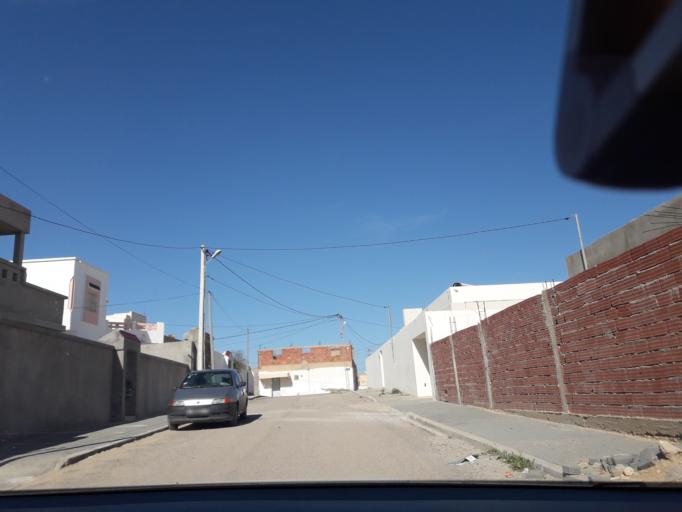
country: TN
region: Safaqis
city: Sfax
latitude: 34.7381
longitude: 10.5218
